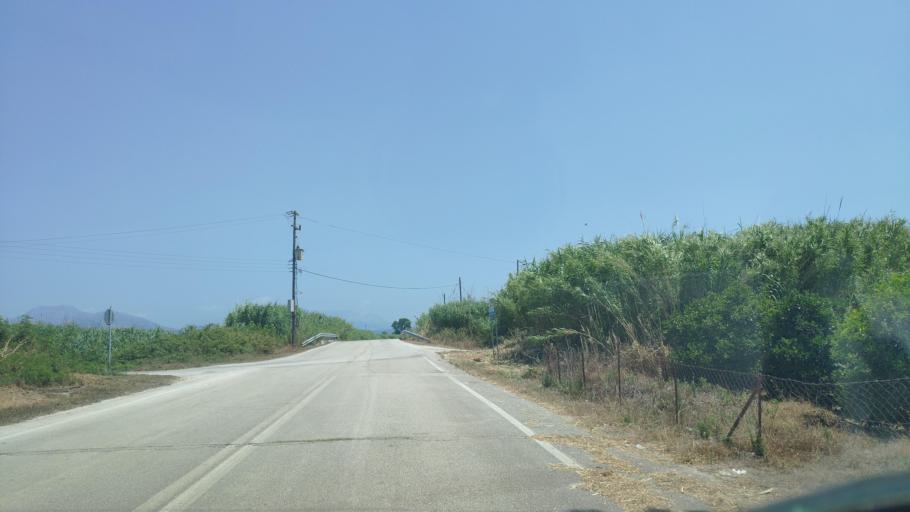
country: GR
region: Epirus
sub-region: Nomos Artas
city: Aneza
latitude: 39.0782
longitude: 20.8855
